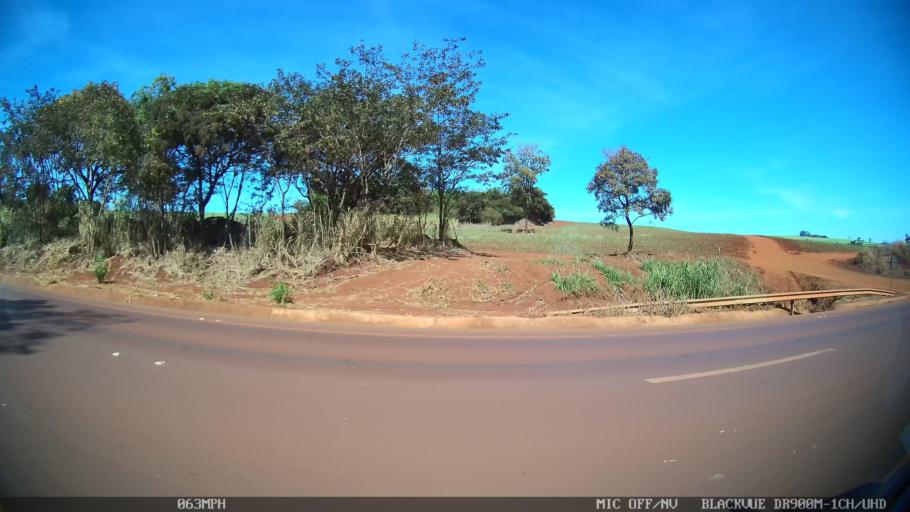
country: BR
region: Sao Paulo
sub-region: Sao Joaquim Da Barra
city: Sao Joaquim da Barra
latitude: -20.5516
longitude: -47.6576
